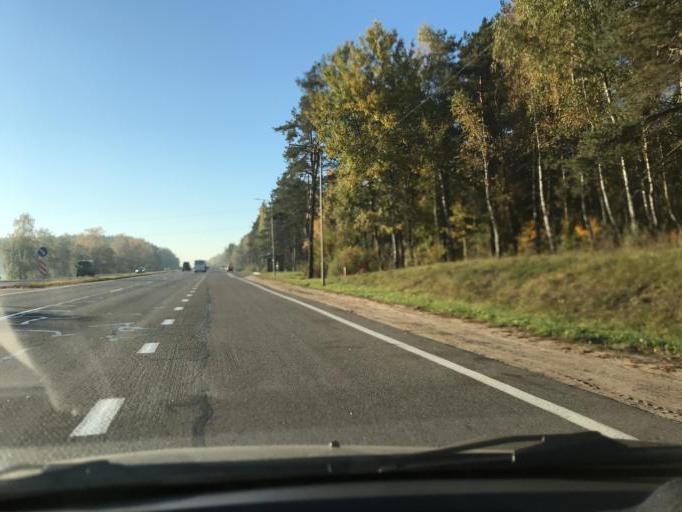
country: BY
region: Minsk
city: Luhavaya Slabada
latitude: 53.7737
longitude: 27.8268
